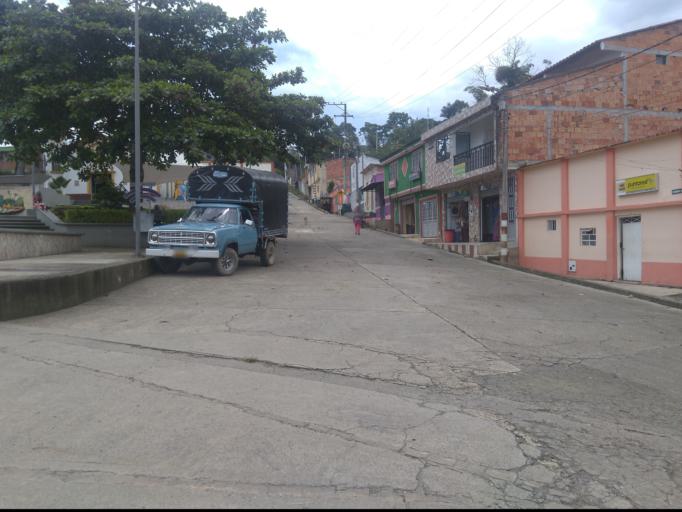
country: CO
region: Santander
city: Florian
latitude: 5.7297
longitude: -73.9330
